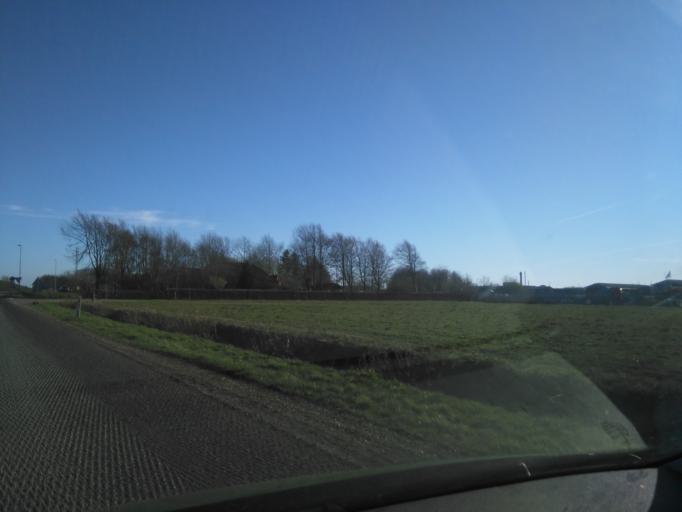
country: DK
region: Central Jutland
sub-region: Ringkobing-Skjern Kommune
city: Videbaek
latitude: 56.0940
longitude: 8.6489
